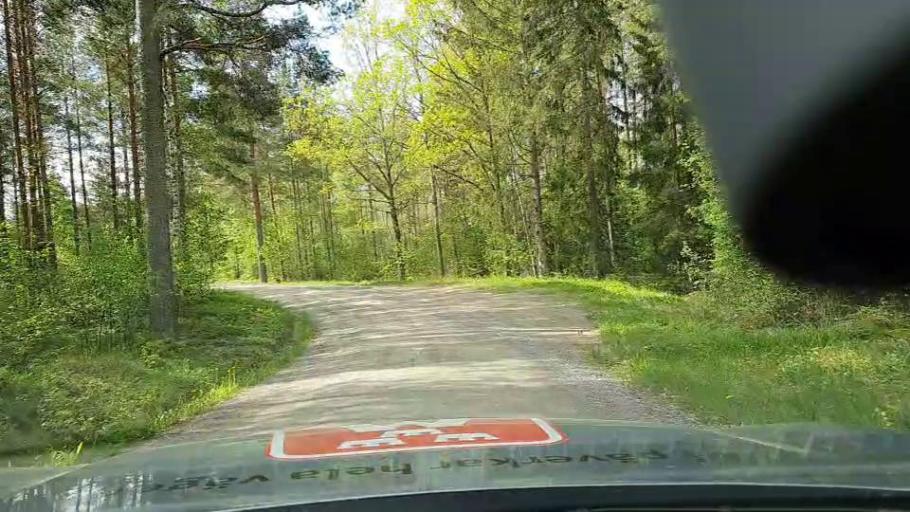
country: SE
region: Soedermanland
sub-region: Flens Kommun
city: Malmkoping
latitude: 59.2606
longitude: 16.8711
